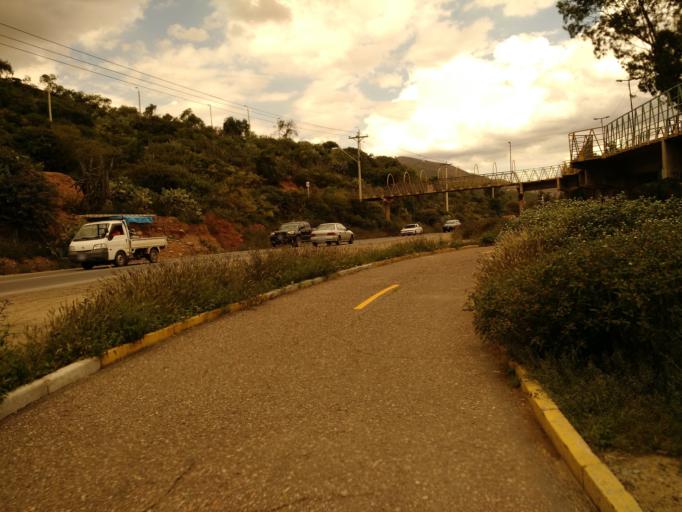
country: BO
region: Cochabamba
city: Cochabamba
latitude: -17.3998
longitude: -66.1344
